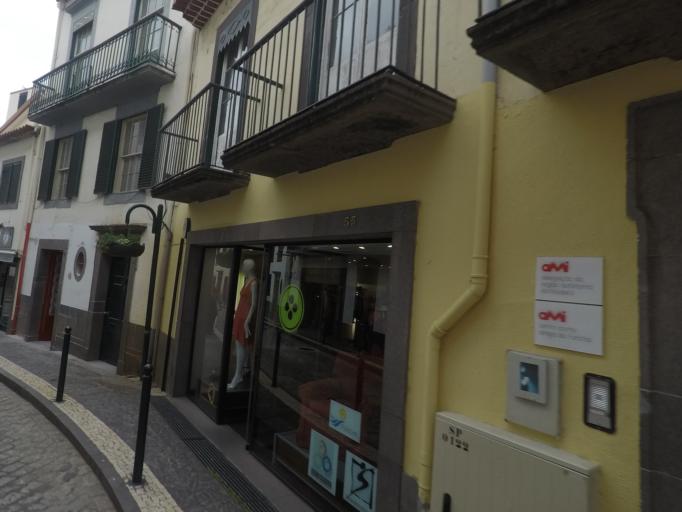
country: PT
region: Madeira
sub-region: Funchal
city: Funchal
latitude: 32.6495
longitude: -16.9114
